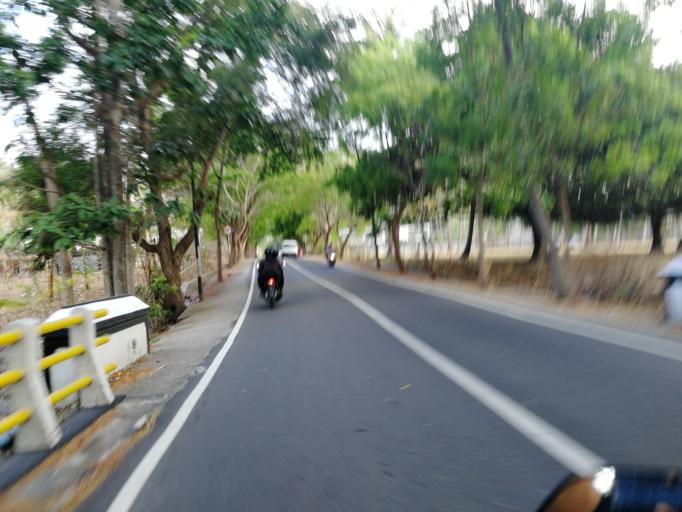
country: ID
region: West Nusa Tenggara
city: Karangsubagan
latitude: -8.4666
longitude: 116.0383
